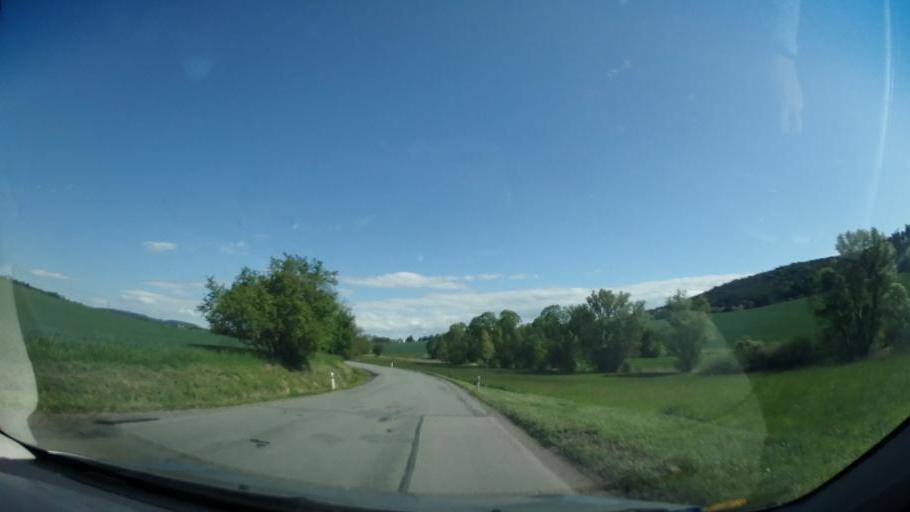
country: CZ
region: South Moravian
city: Velke Opatovice
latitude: 49.6650
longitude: 16.6335
